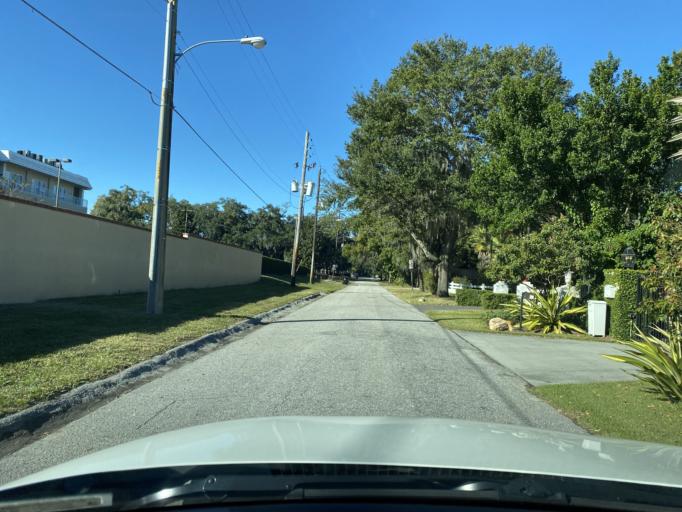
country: US
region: Florida
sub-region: Orange County
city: Orlando
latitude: 28.5537
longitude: -81.3851
